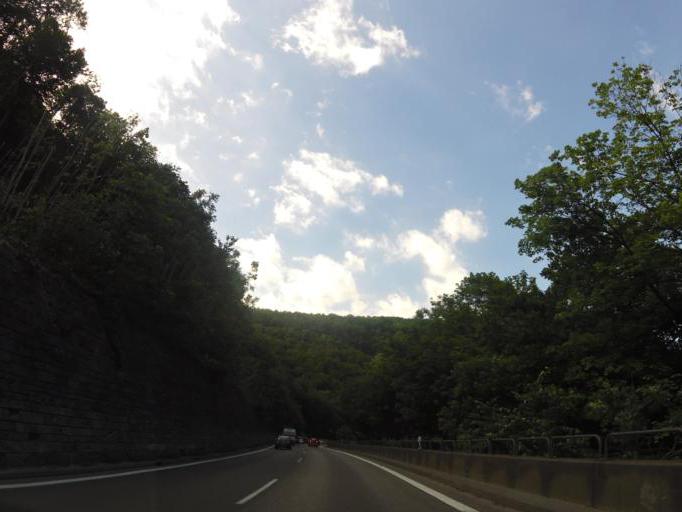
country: DE
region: Baden-Wuerttemberg
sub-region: Regierungsbezirk Stuttgart
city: Muhlhausen
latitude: 48.5688
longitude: 9.6471
